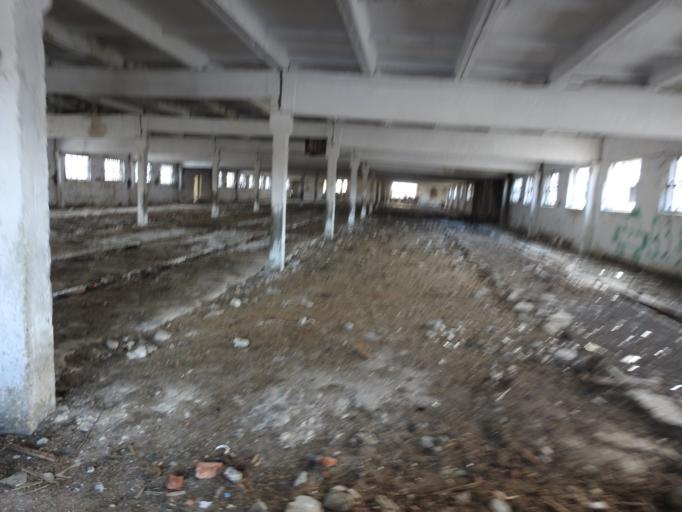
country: RU
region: Saratov
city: Krasnyy Oktyabr'
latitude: 51.3849
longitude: 45.6866
